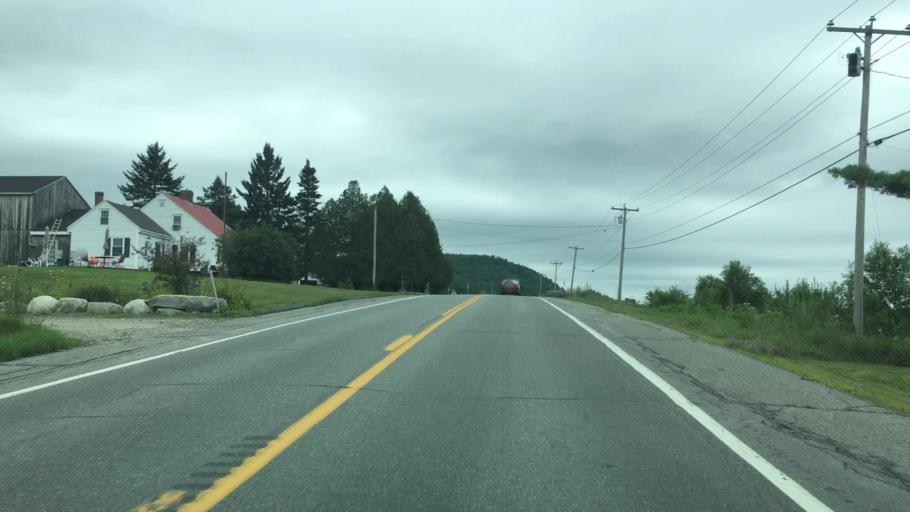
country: US
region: Maine
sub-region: Waldo County
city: Frankfort
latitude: 44.5606
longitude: -68.8662
